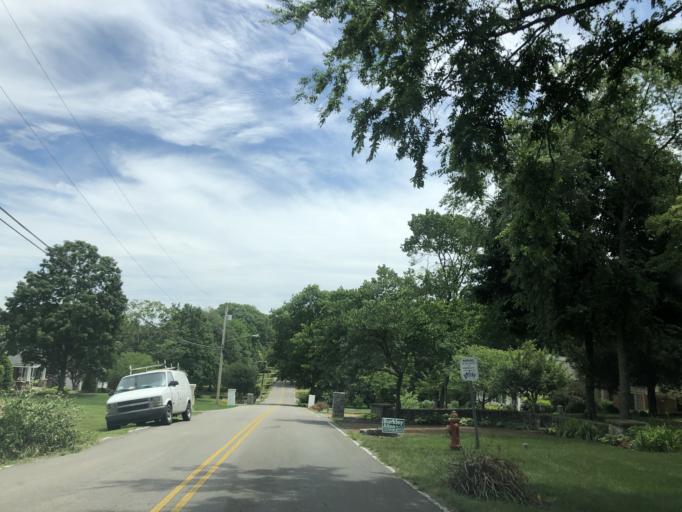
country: US
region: Tennessee
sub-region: Davidson County
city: Oak Hill
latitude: 36.1008
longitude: -86.8086
